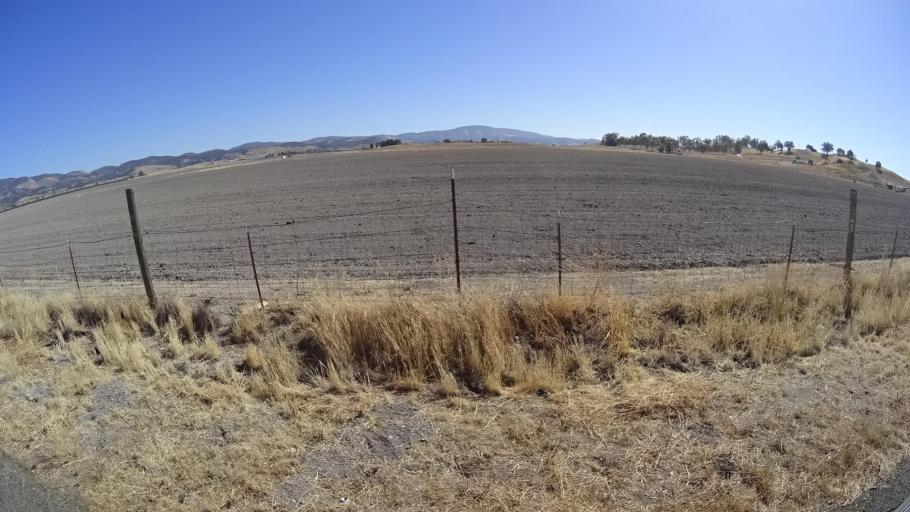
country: US
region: California
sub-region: Monterey County
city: King City
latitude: 35.9584
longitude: -121.1185
